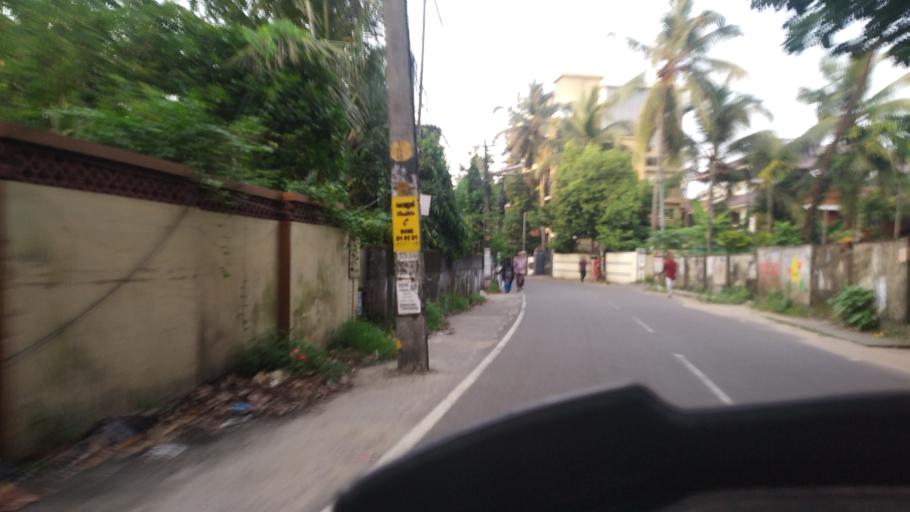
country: IN
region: Kerala
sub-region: Ernakulam
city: Elur
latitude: 10.0260
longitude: 76.2985
